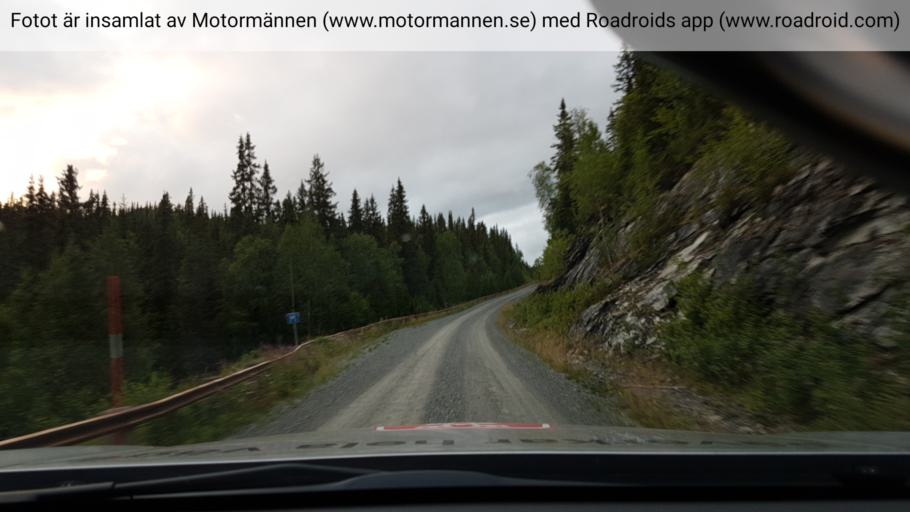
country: SE
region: Vaesterbotten
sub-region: Vilhelmina Kommun
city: Sjoberg
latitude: 65.5326
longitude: 15.4350
